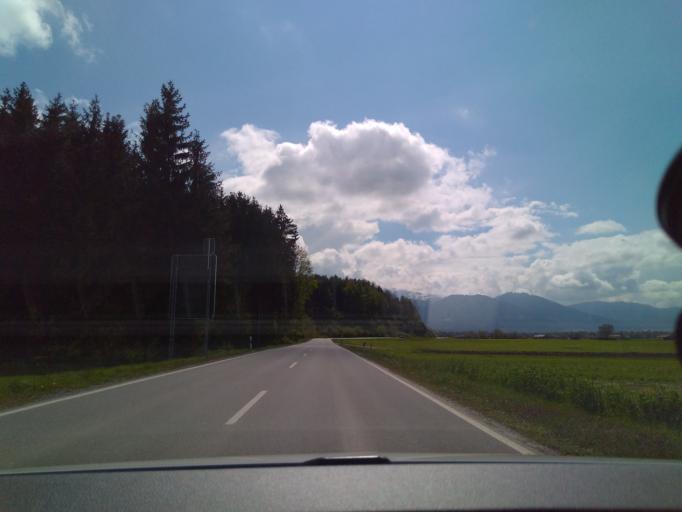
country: DE
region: Bavaria
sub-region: Upper Bavaria
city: Neubeuern
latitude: 47.7906
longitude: 12.1580
